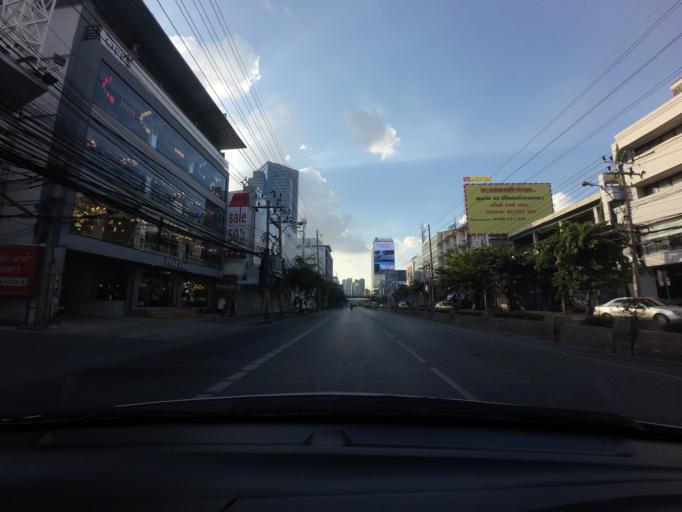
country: TH
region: Bangkok
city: Watthana
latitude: 13.7465
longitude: 100.5767
